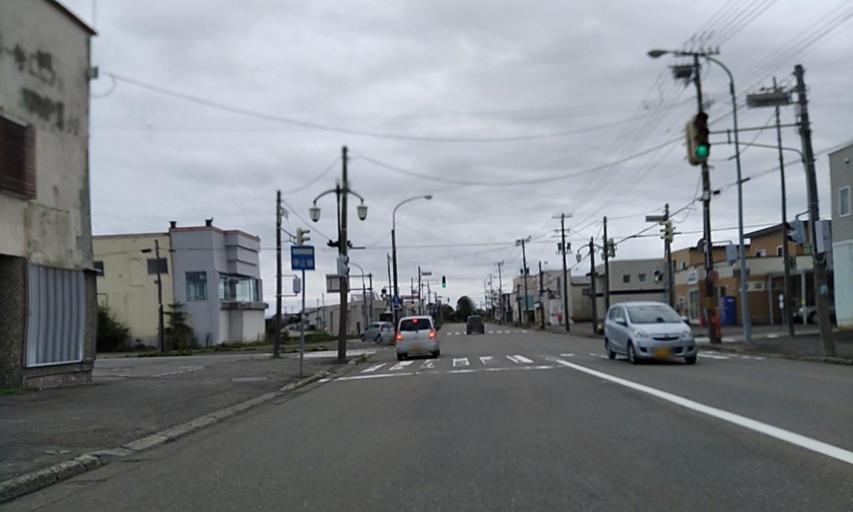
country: JP
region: Hokkaido
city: Obihiro
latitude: 42.2869
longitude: 143.3168
